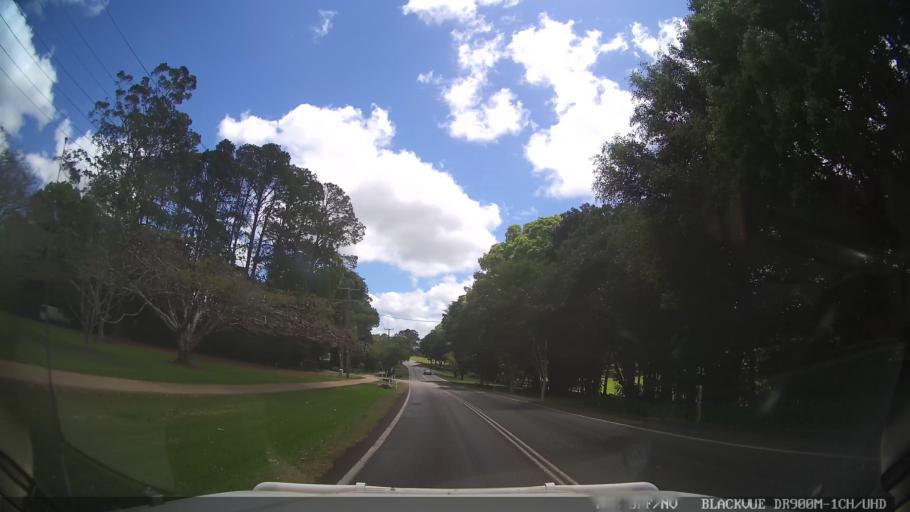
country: AU
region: Queensland
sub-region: Sunshine Coast
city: Nambour
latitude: -26.6603
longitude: 152.8831
